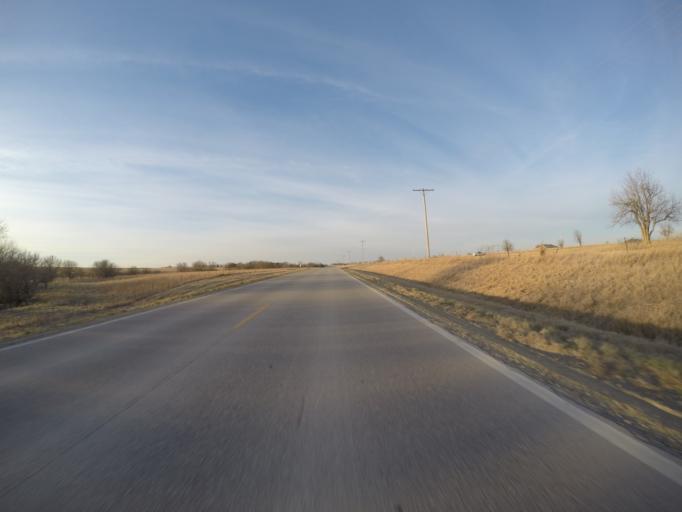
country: US
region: Kansas
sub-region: Riley County
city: Fort Riley North
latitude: 39.3158
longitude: -96.8307
